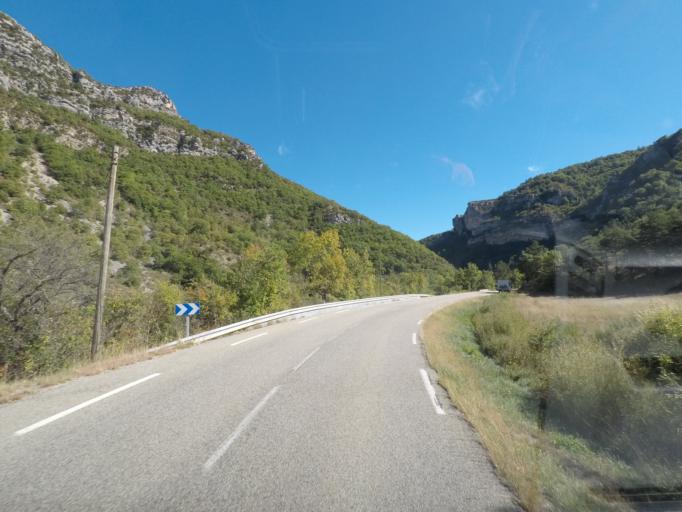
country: FR
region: Rhone-Alpes
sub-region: Departement de la Drome
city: Buis-les-Baronnies
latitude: 44.3924
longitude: 5.3675
